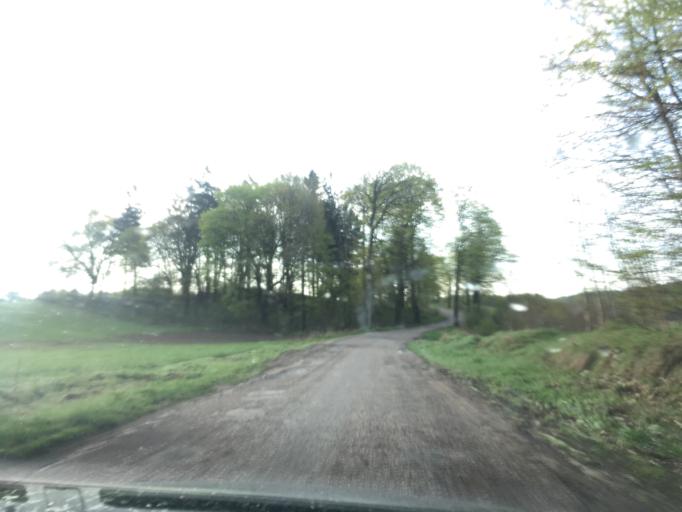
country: PL
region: Warmian-Masurian Voivodeship
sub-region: Powiat ostrodzki
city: Dabrowno
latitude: 53.4331
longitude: 19.9974
